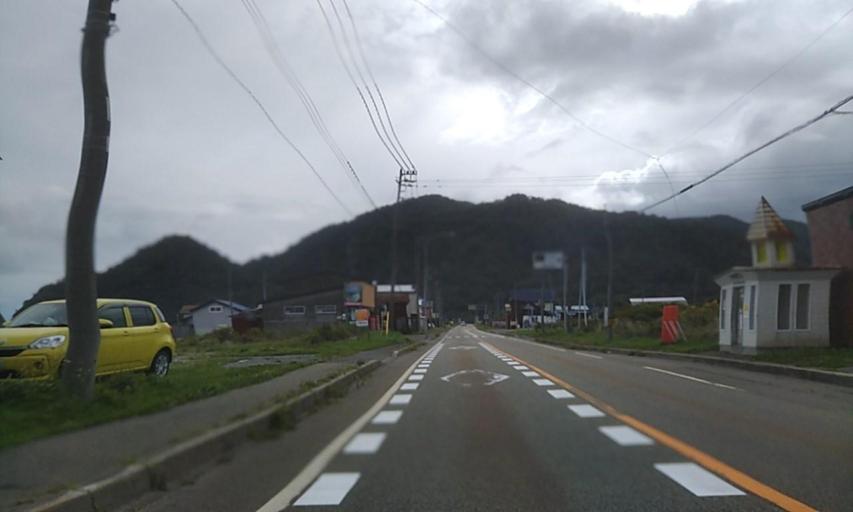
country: JP
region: Hokkaido
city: Obihiro
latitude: 42.1276
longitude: 143.3174
